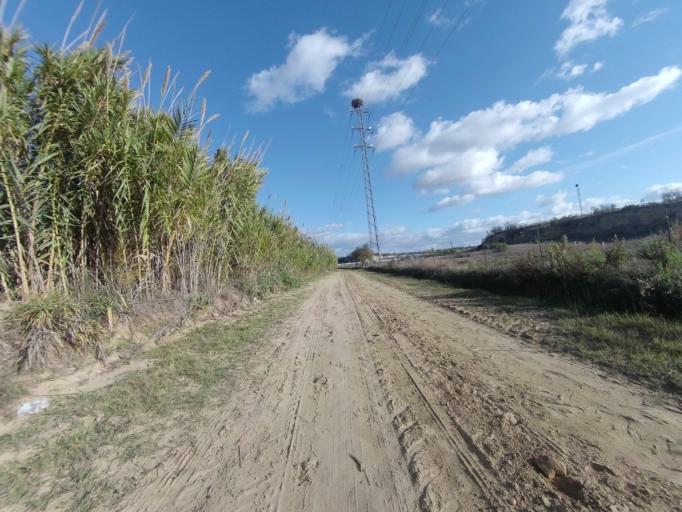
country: ES
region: Andalusia
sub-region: Provincia de Huelva
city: Moguer
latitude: 37.2661
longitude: -6.8602
